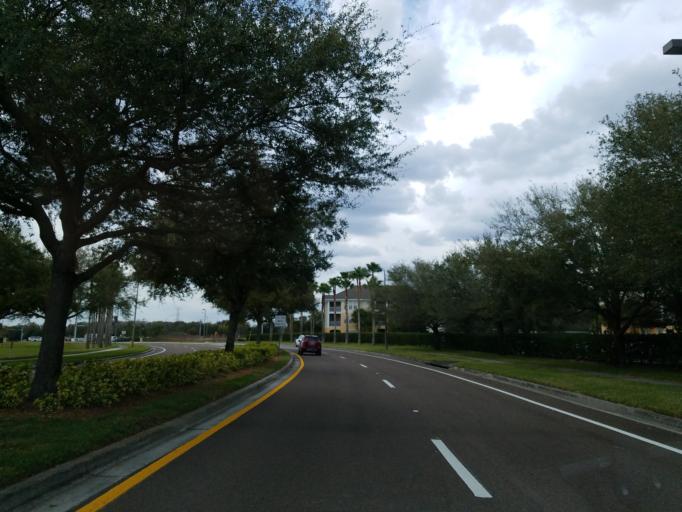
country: US
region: Florida
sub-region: Hillsborough County
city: Palm River-Clair Mel
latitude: 27.9347
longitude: -82.3495
